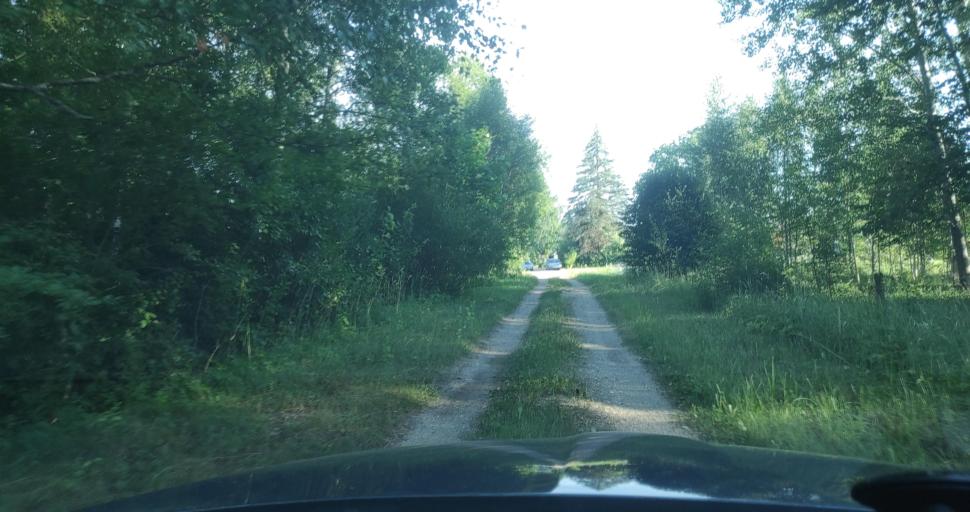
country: LV
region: Skrunda
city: Skrunda
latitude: 56.6739
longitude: 21.9957
